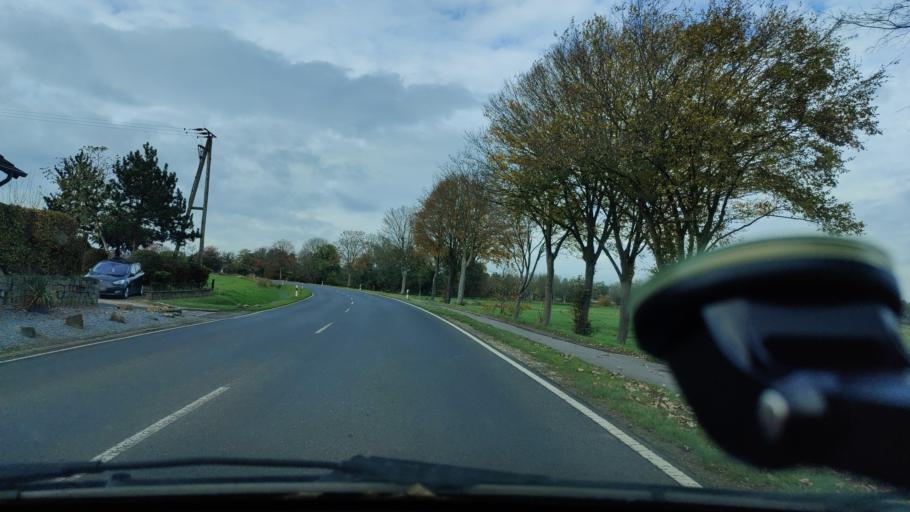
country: DE
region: North Rhine-Westphalia
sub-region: Regierungsbezirk Dusseldorf
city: Sonsbeck
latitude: 51.6395
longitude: 6.3919
